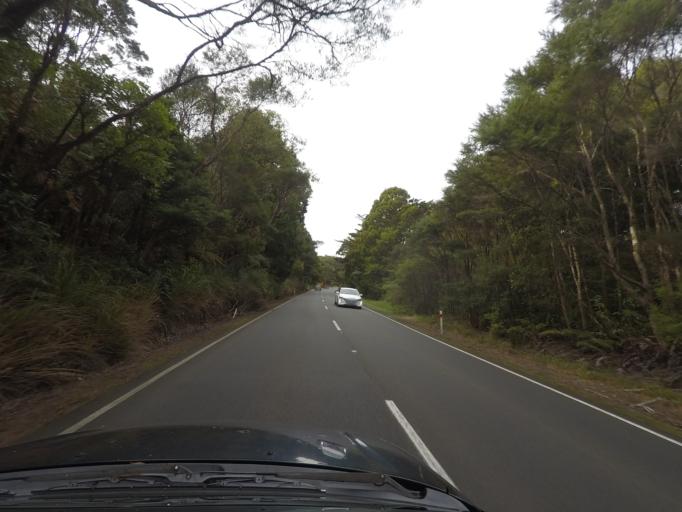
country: NZ
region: Auckland
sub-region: Auckland
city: Titirangi
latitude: -36.9330
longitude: 174.5682
